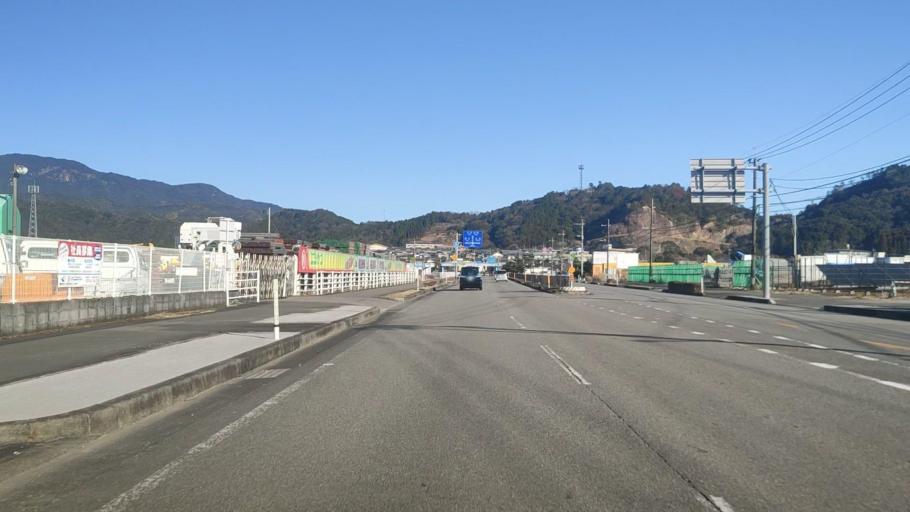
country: JP
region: Miyazaki
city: Nobeoka
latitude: 32.6060
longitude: 131.6829
